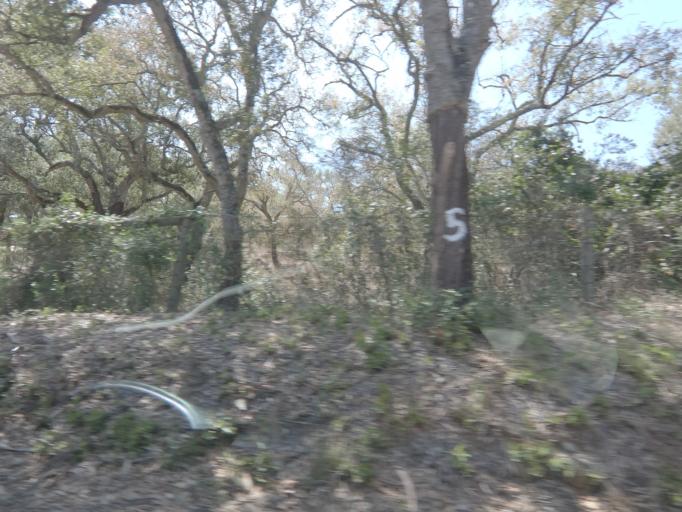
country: PT
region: Setubal
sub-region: Setubal
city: Setubal
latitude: 38.5201
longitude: -8.9309
